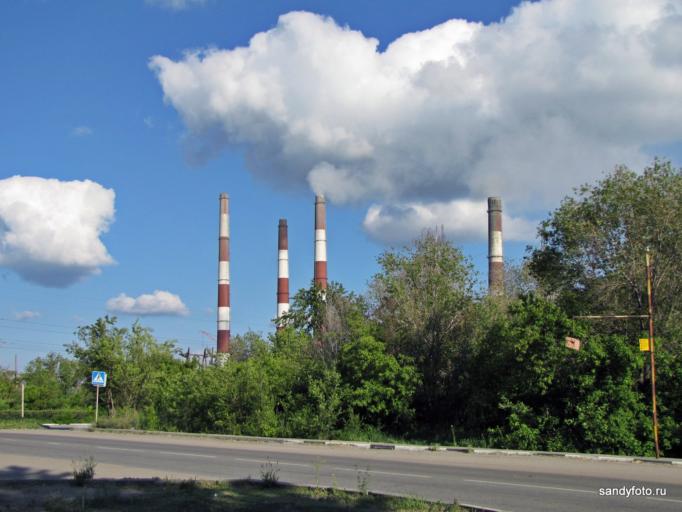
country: RU
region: Chelyabinsk
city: Troitsk
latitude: 54.0415
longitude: 61.6391
